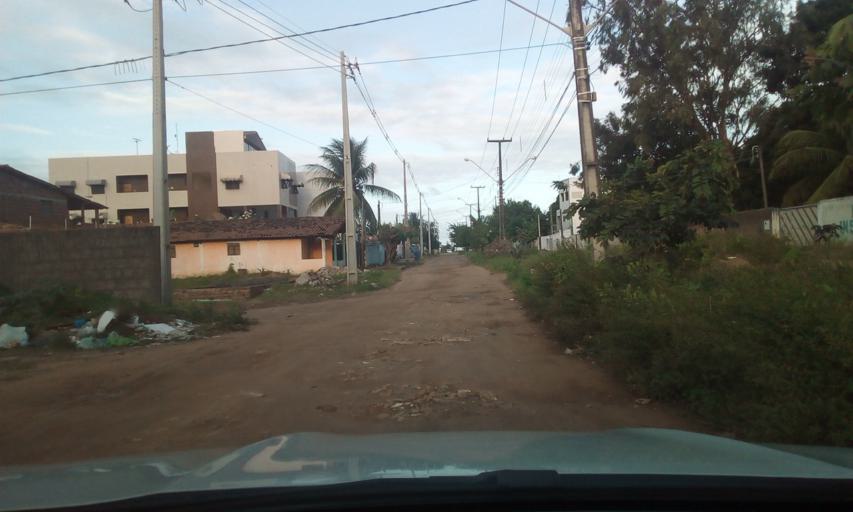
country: BR
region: Paraiba
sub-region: Joao Pessoa
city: Joao Pessoa
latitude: -7.1602
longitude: -34.8241
